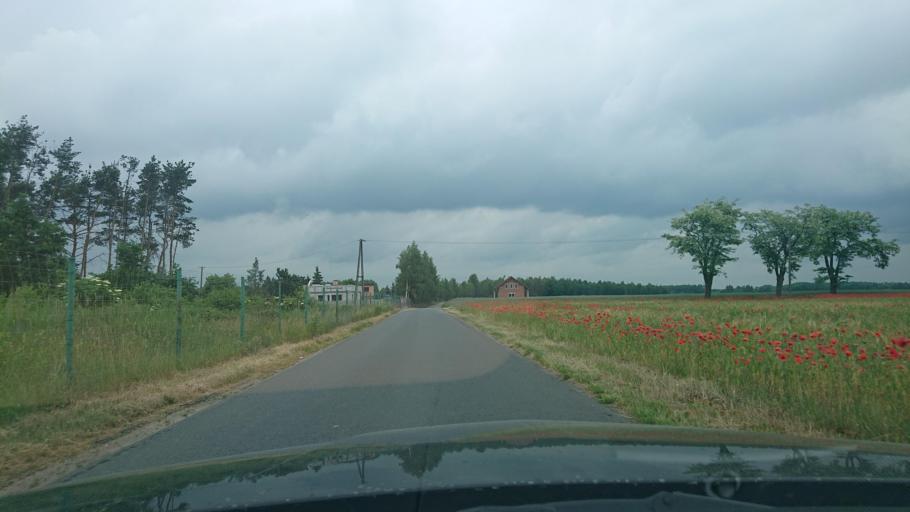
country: PL
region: Greater Poland Voivodeship
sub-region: Powiat gnieznienski
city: Gniezno
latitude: 52.4806
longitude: 17.5388
